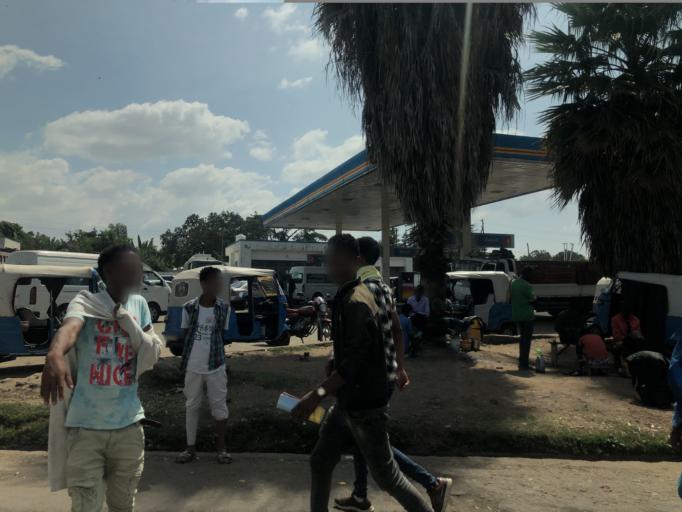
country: ET
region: Oromiya
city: Shashemene
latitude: 7.2100
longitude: 38.6151
